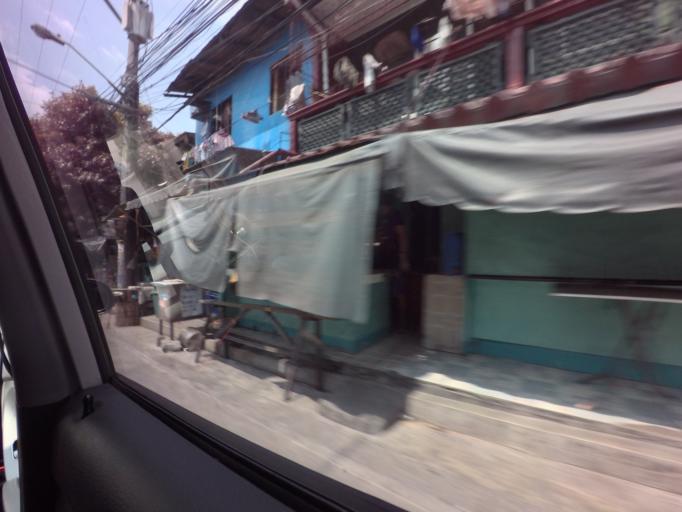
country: PH
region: Metro Manila
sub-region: San Juan
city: San Juan
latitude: 14.5932
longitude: 121.0240
